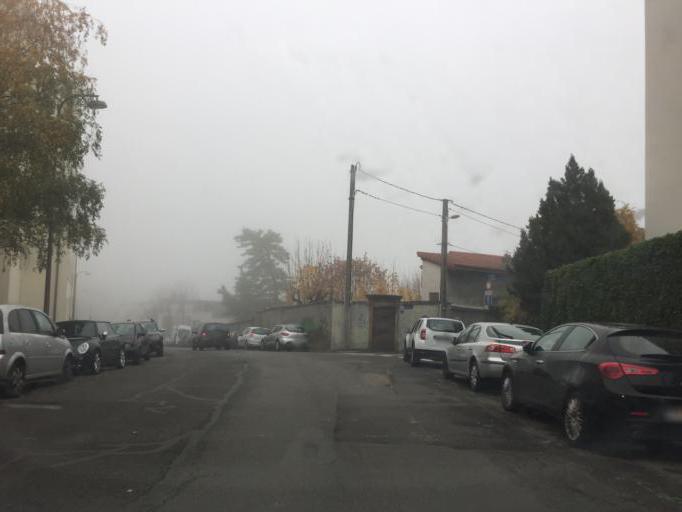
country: FR
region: Rhone-Alpes
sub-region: Departement du Rhone
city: Caluire-et-Cuire
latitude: 45.7842
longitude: 4.8239
